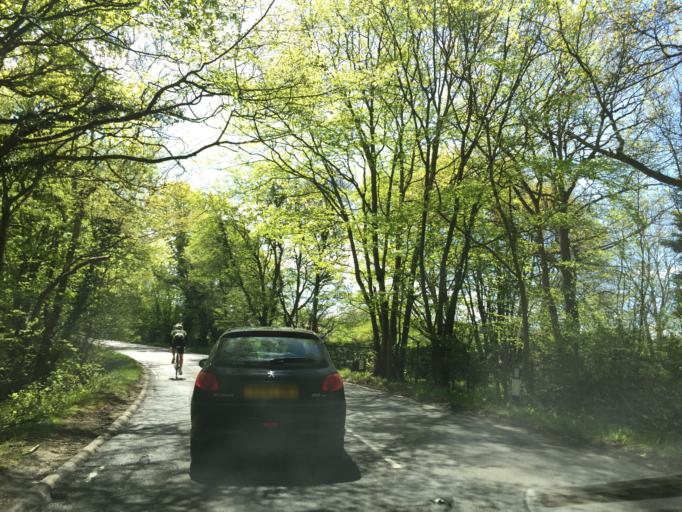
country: GB
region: England
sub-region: Kent
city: Edenbridge
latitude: 51.1335
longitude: 0.1070
